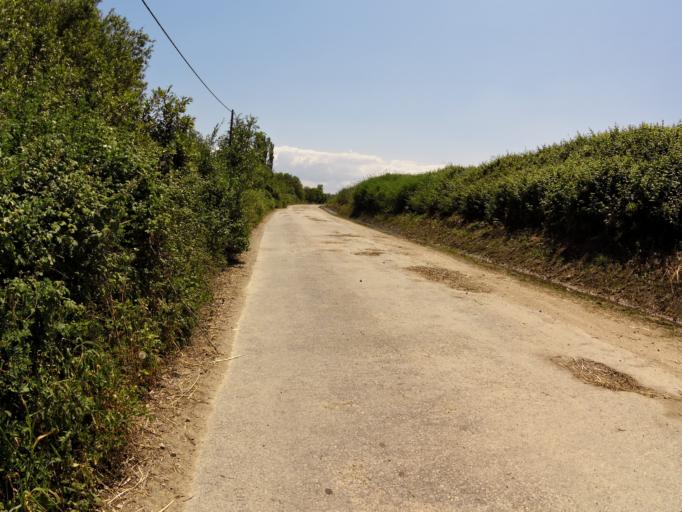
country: PT
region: Coimbra
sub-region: Montemor-O-Velho
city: Montemor-o-Velho
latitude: 40.1488
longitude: -8.7175
